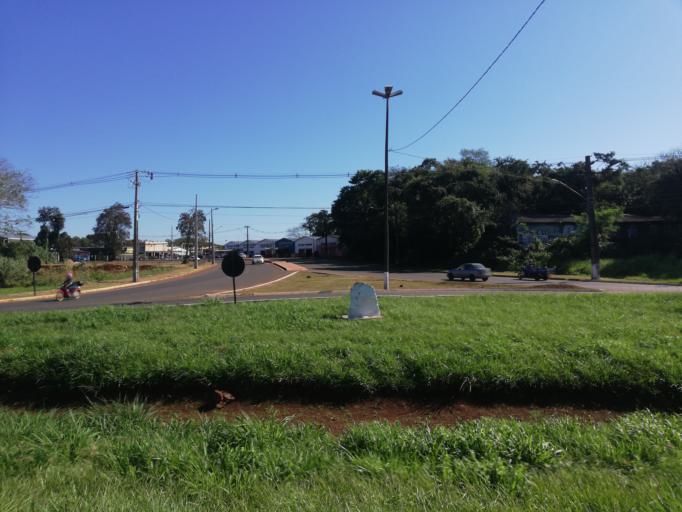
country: AR
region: Misiones
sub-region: Departamento de Iguazu
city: Puerto Iguazu
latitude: -25.5770
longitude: -54.5548
